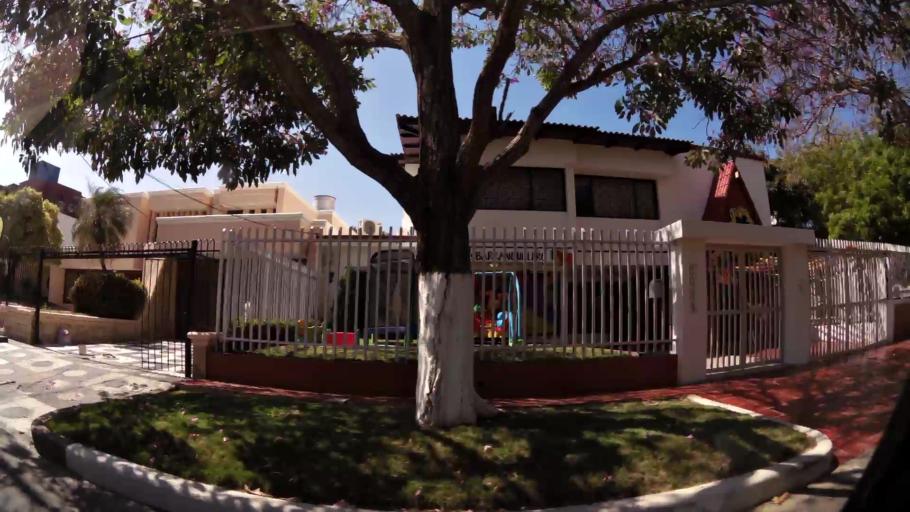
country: CO
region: Atlantico
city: Barranquilla
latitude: 11.0145
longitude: -74.8155
